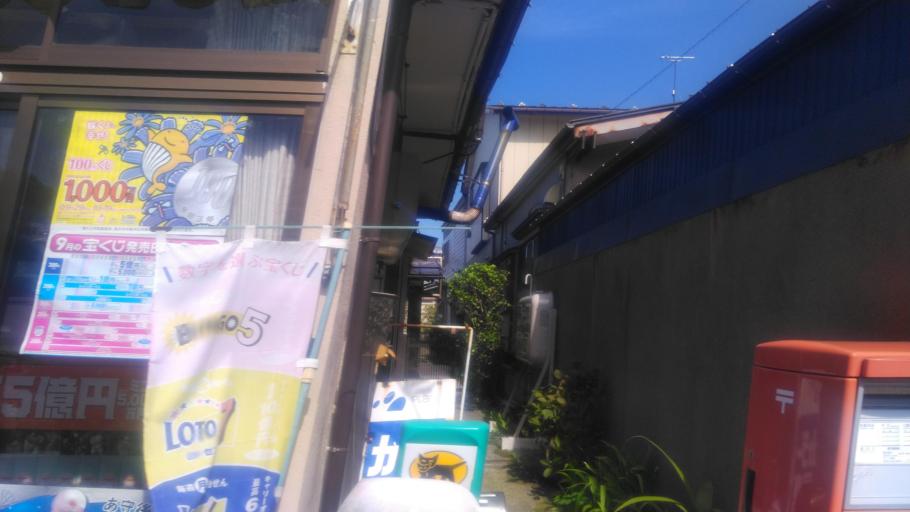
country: JP
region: Akita
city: Noshiromachi
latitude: 40.2036
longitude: 140.0294
